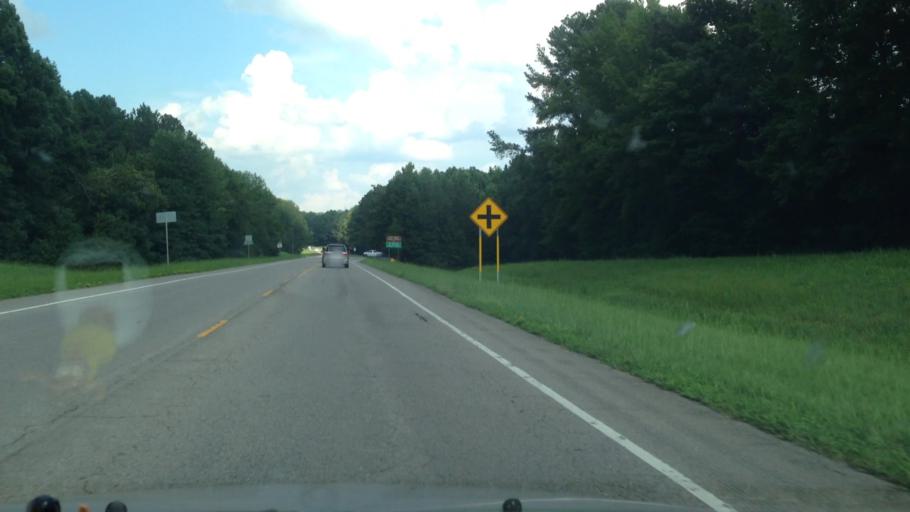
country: US
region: North Carolina
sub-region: Lee County
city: Broadway
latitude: 35.4388
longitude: -79.0696
